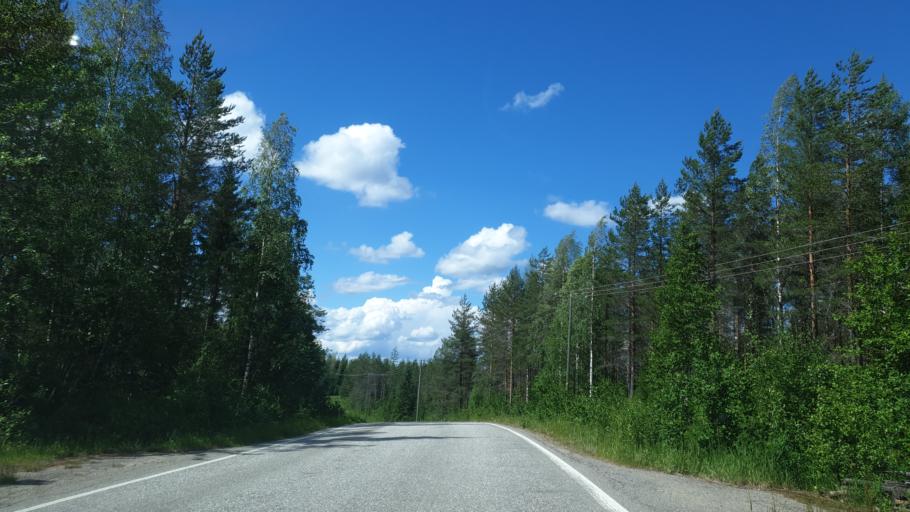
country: FI
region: Northern Savo
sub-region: Koillis-Savo
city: Kaavi
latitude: 63.0404
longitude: 28.5968
